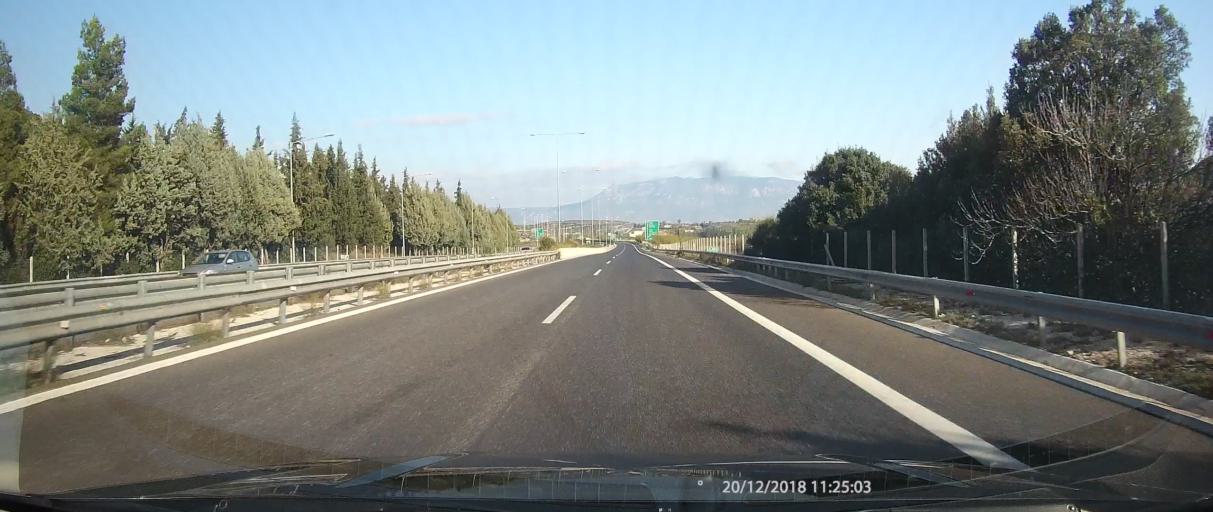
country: GR
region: Peloponnese
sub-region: Nomos Korinthias
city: Arkhaia Korinthos
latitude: 37.8892
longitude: 22.8946
